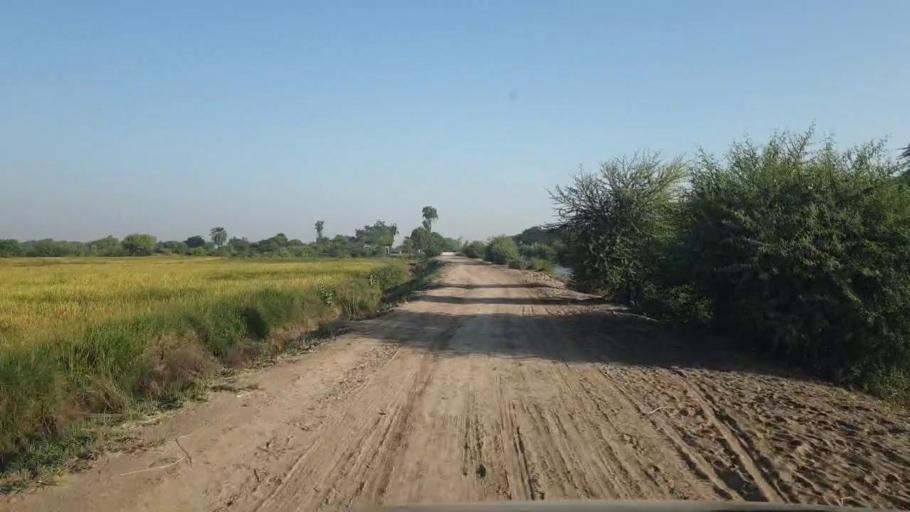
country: PK
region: Sindh
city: Badin
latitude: 24.6865
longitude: 68.8156
